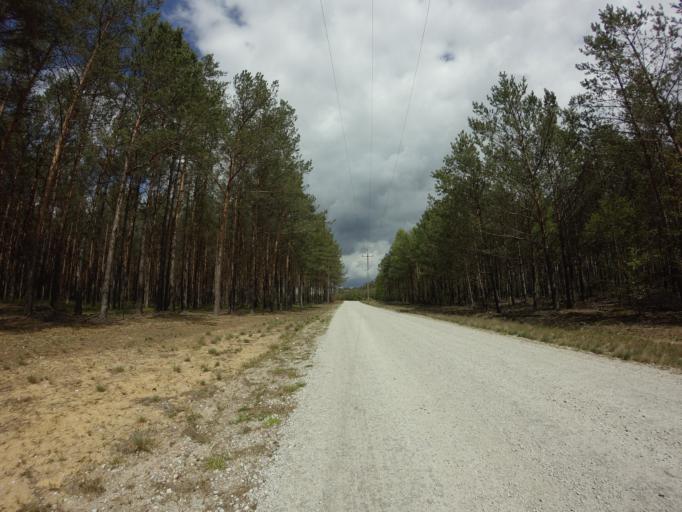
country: PL
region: West Pomeranian Voivodeship
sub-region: Powiat drawski
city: Kalisz Pomorski
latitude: 53.1911
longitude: 15.9736
